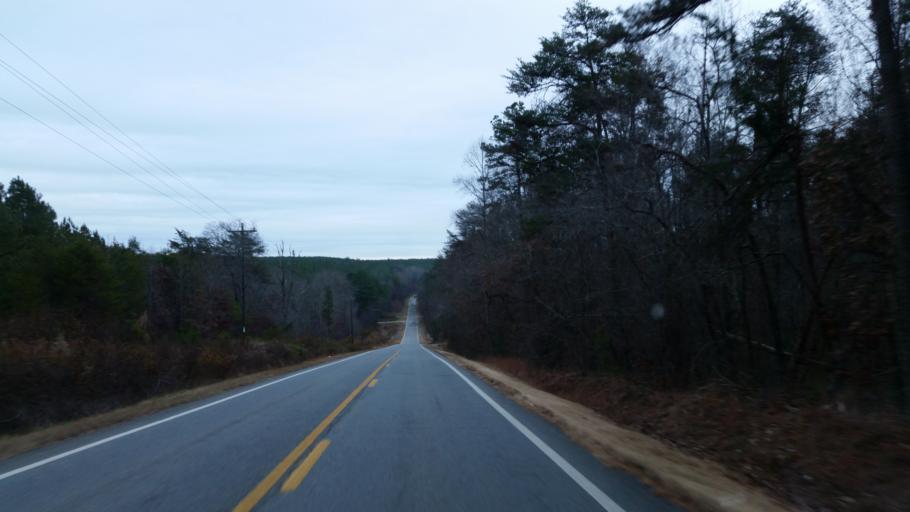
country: US
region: Georgia
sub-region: Dawson County
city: Dawsonville
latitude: 34.4524
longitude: -84.1301
